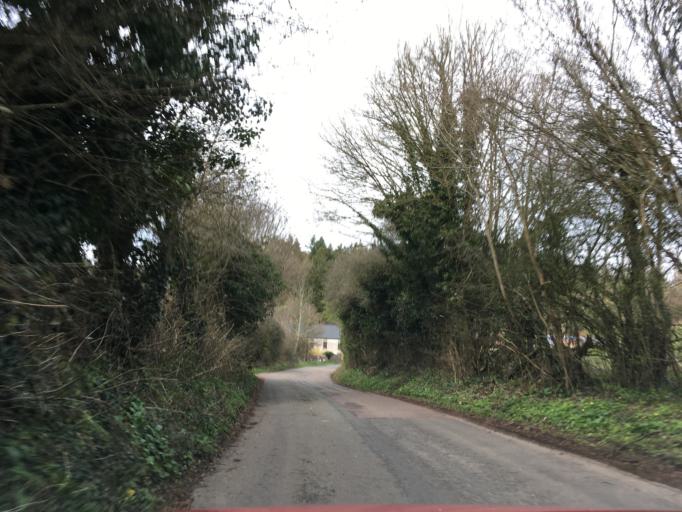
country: GB
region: England
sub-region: Gloucestershire
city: Coleford
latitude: 51.7848
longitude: -2.6314
